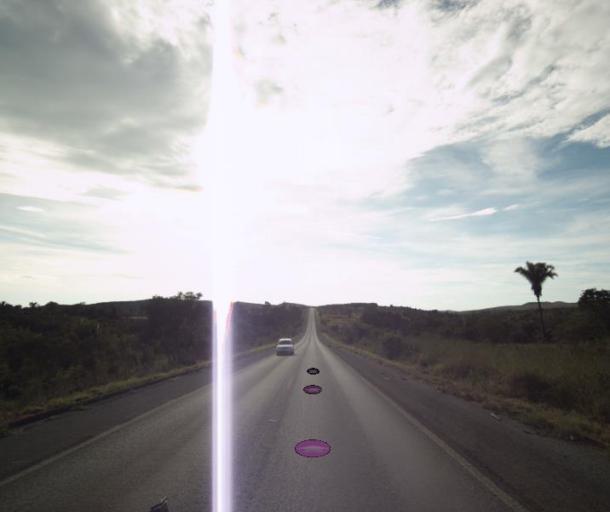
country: BR
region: Goias
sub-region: Pirenopolis
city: Pirenopolis
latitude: -15.7510
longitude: -48.6306
